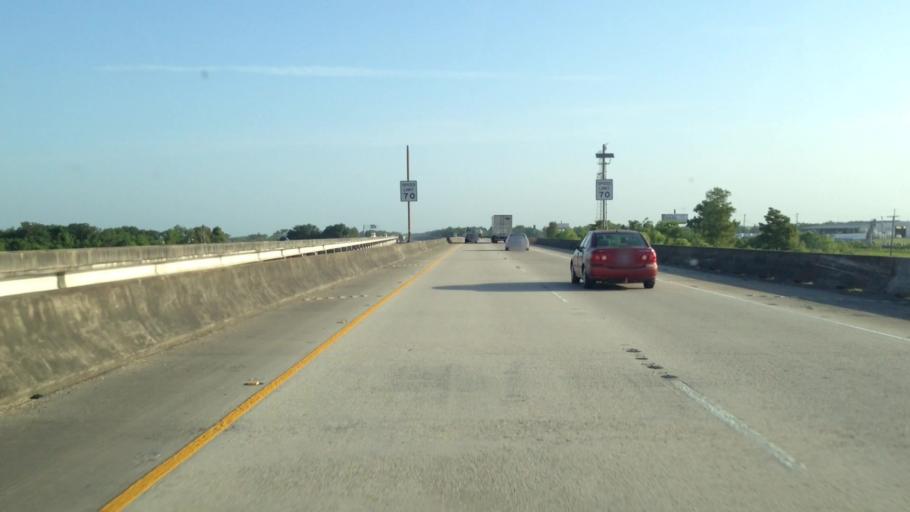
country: US
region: Louisiana
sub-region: Tangipahoa Parish
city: Ponchatoula
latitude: 30.3087
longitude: -90.4065
